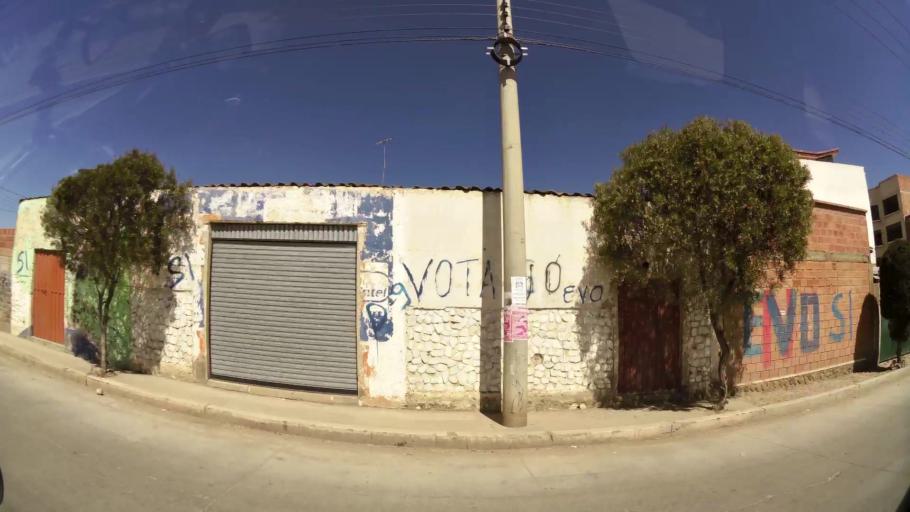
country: BO
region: La Paz
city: La Paz
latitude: -16.5485
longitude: -68.1925
